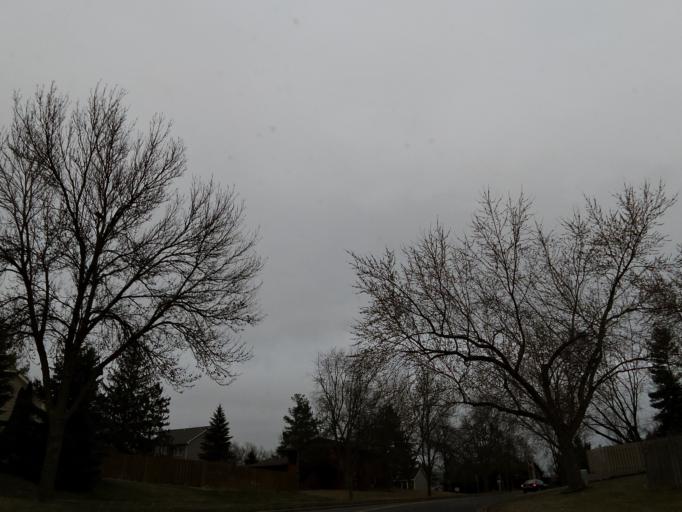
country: US
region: Wisconsin
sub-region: Saint Croix County
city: Hudson
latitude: 44.9694
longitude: -92.7341
